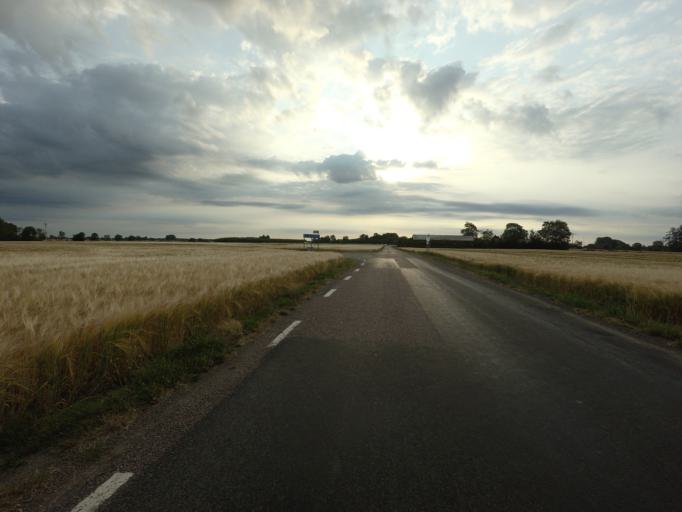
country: SE
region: Skane
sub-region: Hoganas Kommun
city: Hoganas
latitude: 56.1521
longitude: 12.6275
